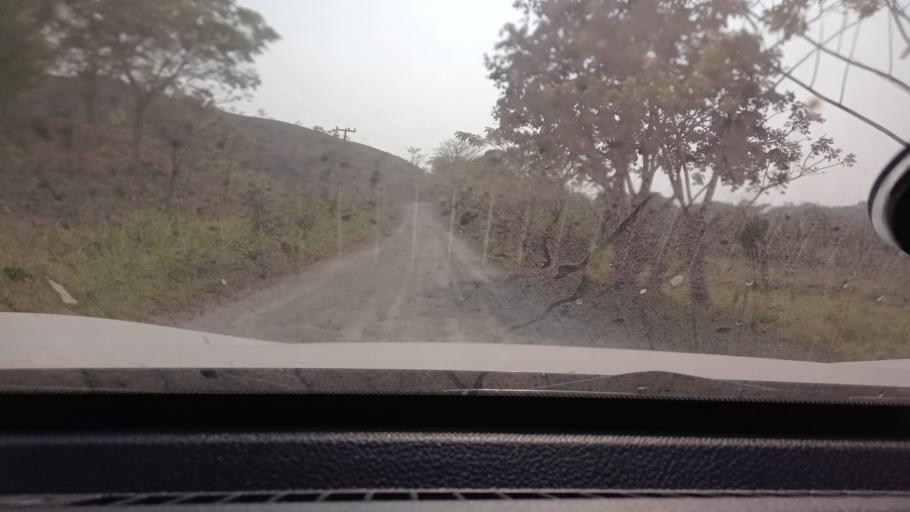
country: MX
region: Tabasco
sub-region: Huimanguillo
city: Francisco Rueda
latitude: 17.6205
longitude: -93.9446
